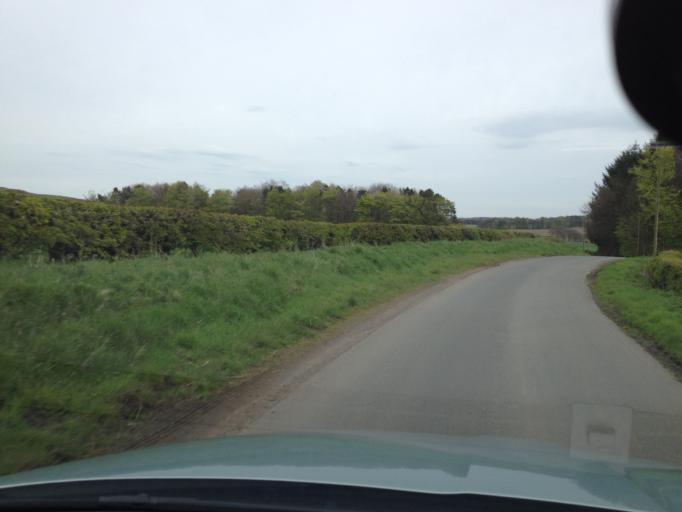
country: GB
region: Scotland
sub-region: West Lothian
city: Linlithgow
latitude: 55.9360
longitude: -3.5935
